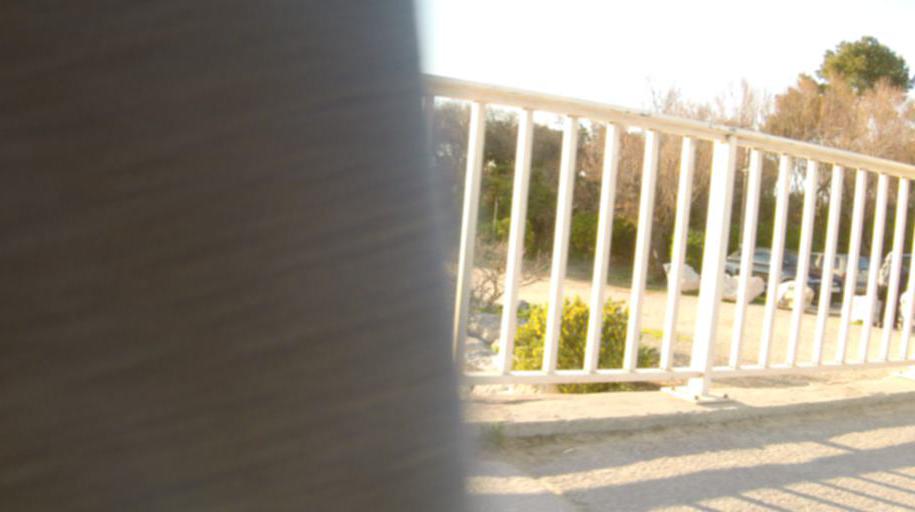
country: FR
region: Provence-Alpes-Cote d'Azur
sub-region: Departement des Bouches-du-Rhone
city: Marseille 08
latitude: 43.2605
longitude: 5.3751
